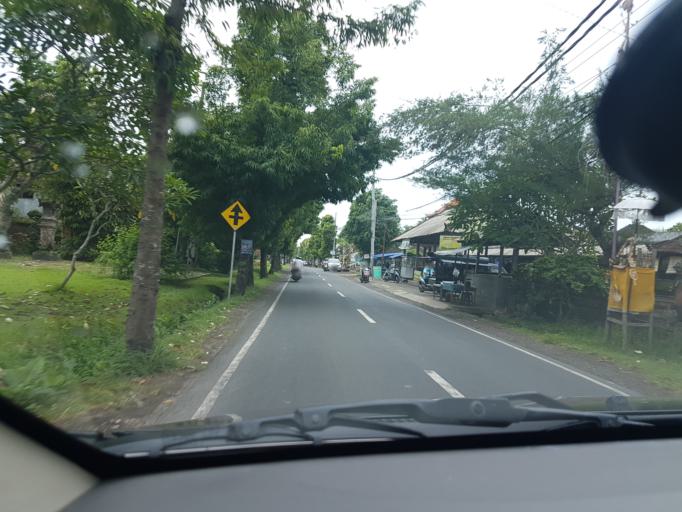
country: ID
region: Bali
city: Banjar Pande
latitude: -8.5103
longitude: 115.2413
